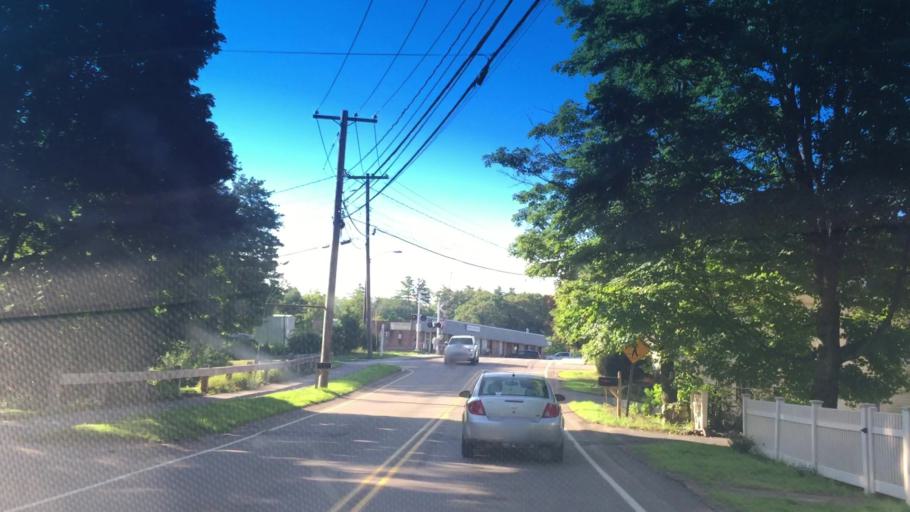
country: US
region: Massachusetts
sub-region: Norfolk County
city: Norfolk
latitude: 42.1211
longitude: -71.3258
